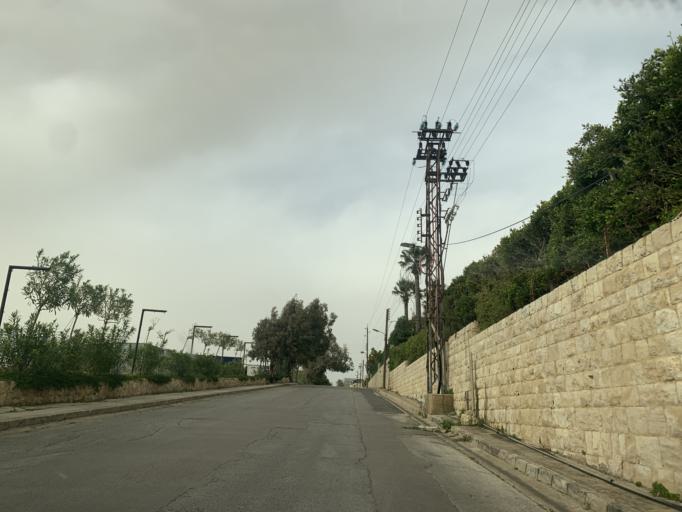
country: LB
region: Mont-Liban
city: Jbail
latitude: 34.1030
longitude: 35.6517
